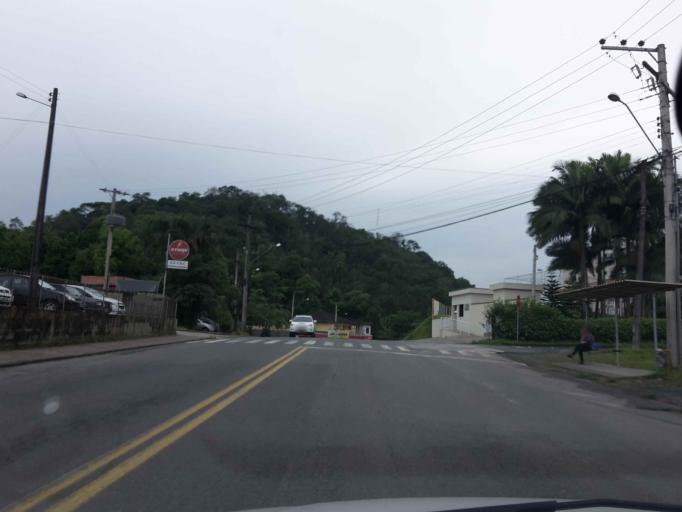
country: BR
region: Santa Catarina
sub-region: Blumenau
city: Blumenau
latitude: -26.8571
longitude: -49.1082
